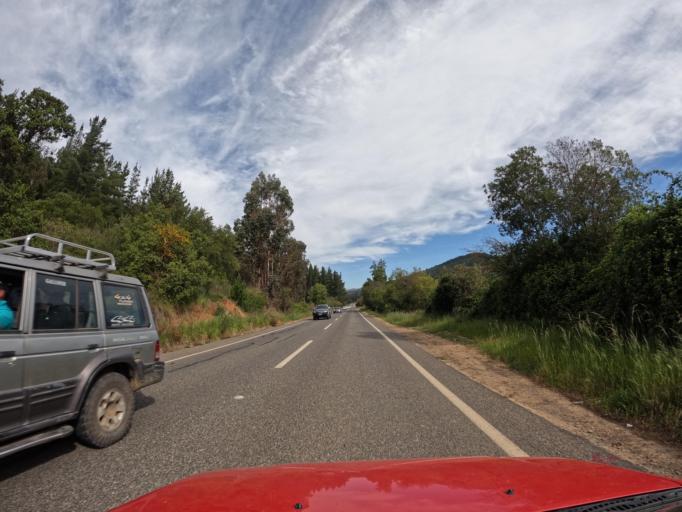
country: CL
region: Maule
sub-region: Provincia de Talca
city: Talca
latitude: -35.3114
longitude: -71.9626
